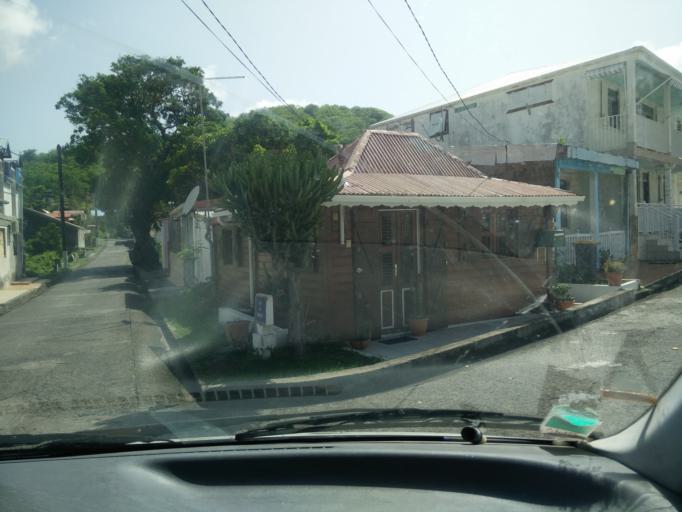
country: GP
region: Guadeloupe
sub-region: Guadeloupe
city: Terre-de-Bas
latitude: 15.8501
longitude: -61.6442
